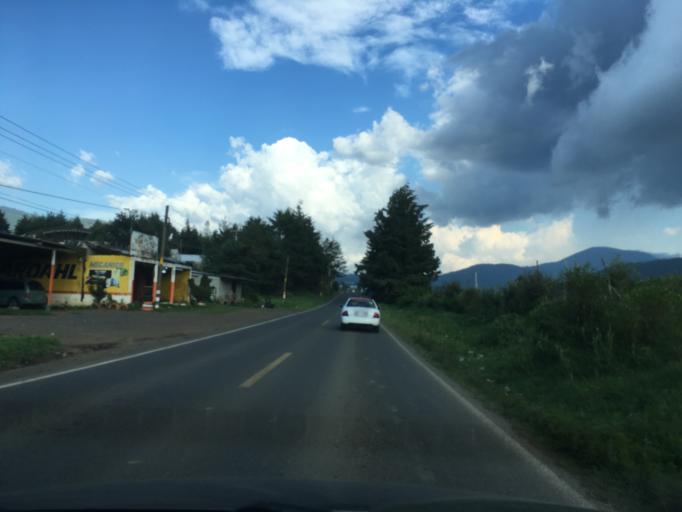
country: MX
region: Michoacan
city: Nahuatzen
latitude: 19.6595
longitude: -101.9310
